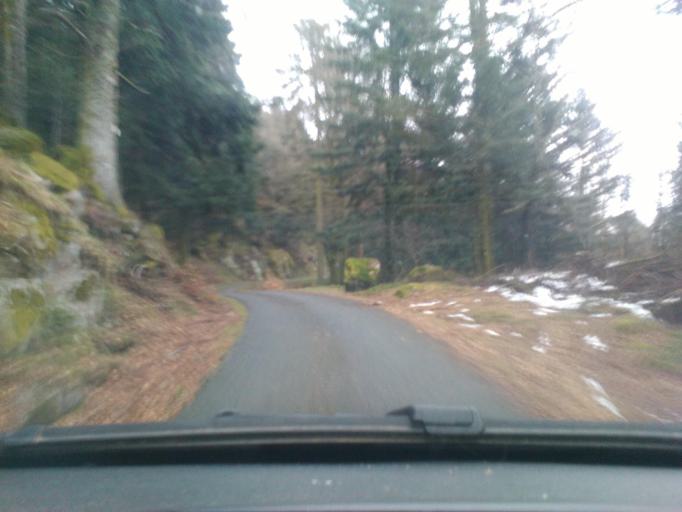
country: FR
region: Lorraine
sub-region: Departement des Vosges
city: Gerardmer
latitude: 48.1050
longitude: 6.8758
